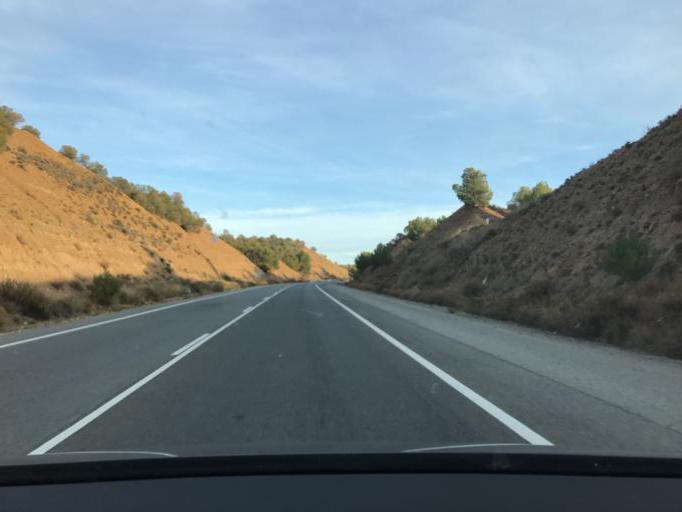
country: ES
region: Andalusia
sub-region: Provincia de Granada
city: Guadix
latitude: 37.2704
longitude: -3.0994
